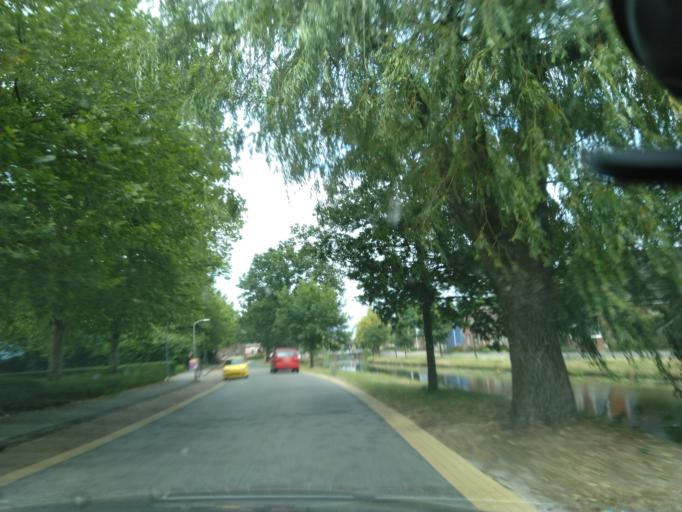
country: NL
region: Groningen
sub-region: Gemeente Pekela
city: Oude Pekela
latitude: 53.0921
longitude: 6.9871
